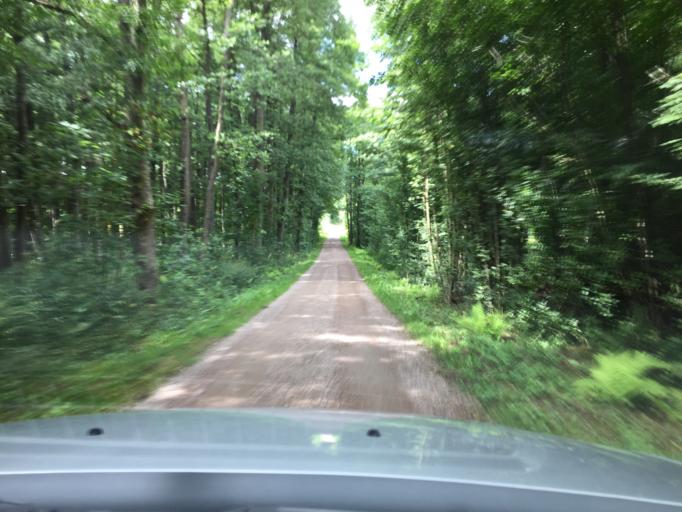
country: SE
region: Skane
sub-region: Hassleholms Kommun
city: Sosdala
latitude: 56.0256
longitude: 13.6432
